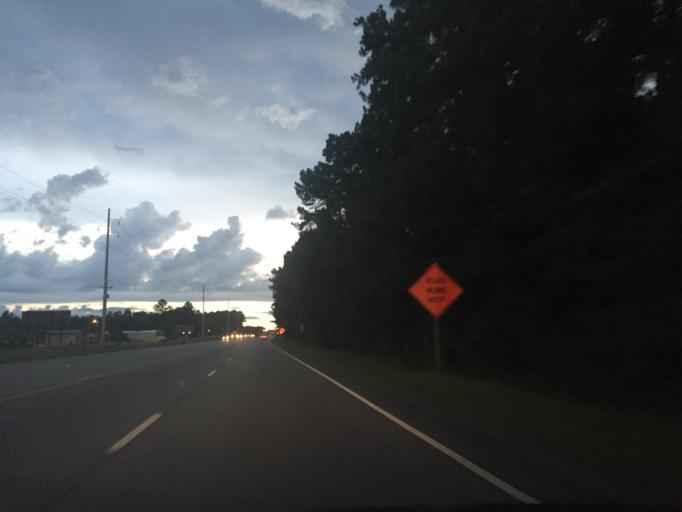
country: US
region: Georgia
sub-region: Liberty County
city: Hinesville
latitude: 31.8339
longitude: -81.5337
